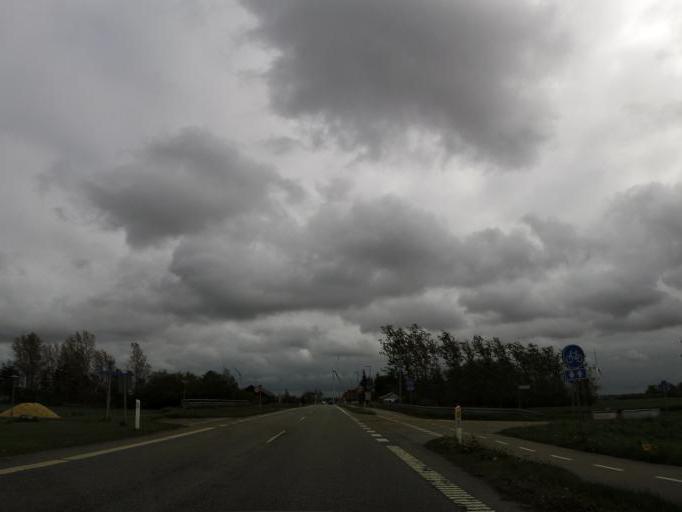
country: DE
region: Schleswig-Holstein
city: Suderlugum
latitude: 54.9069
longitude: 8.9087
